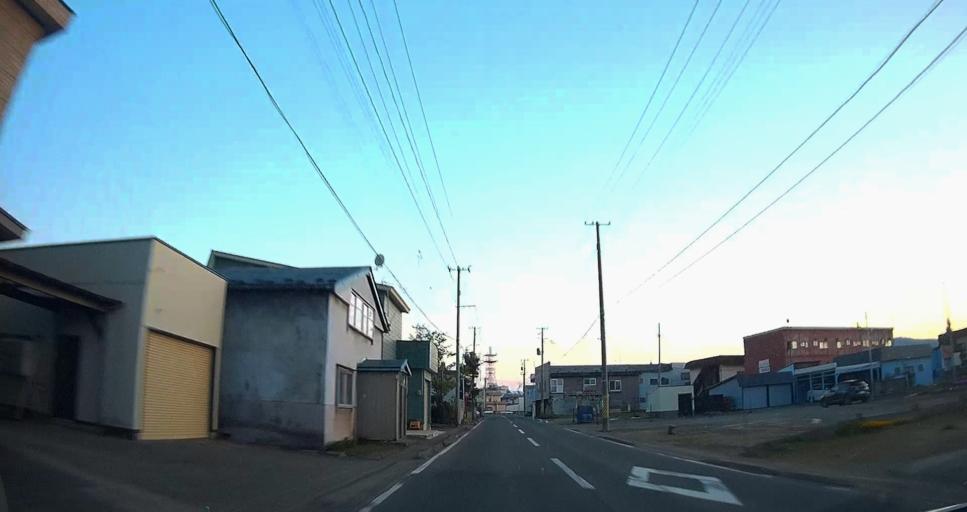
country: JP
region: Aomori
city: Misawa
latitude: 40.8693
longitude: 141.1307
